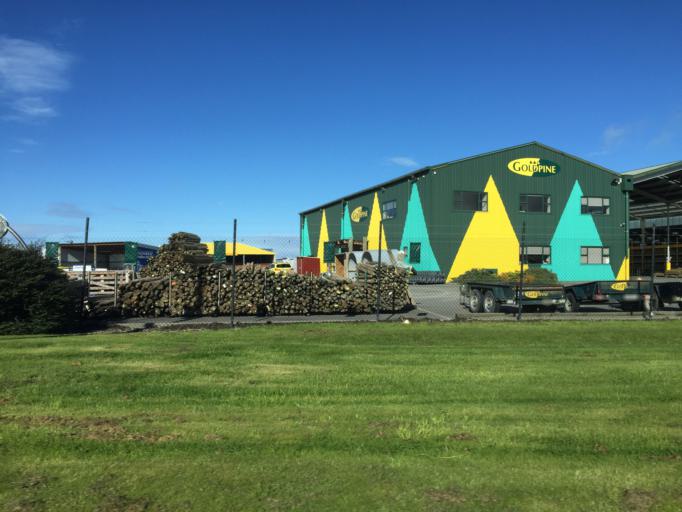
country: NZ
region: Southland
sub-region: Invercargill City
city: Invercargill
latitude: -46.3448
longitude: 168.3466
